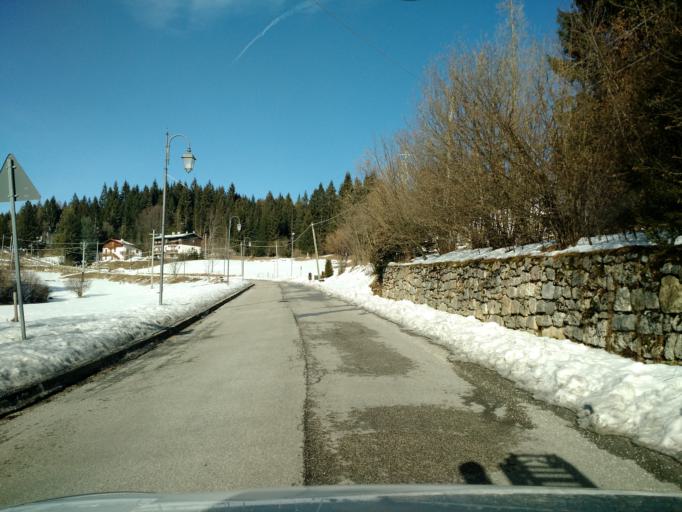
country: IT
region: Veneto
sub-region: Provincia di Vicenza
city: Roana
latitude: 45.8817
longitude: 11.4632
